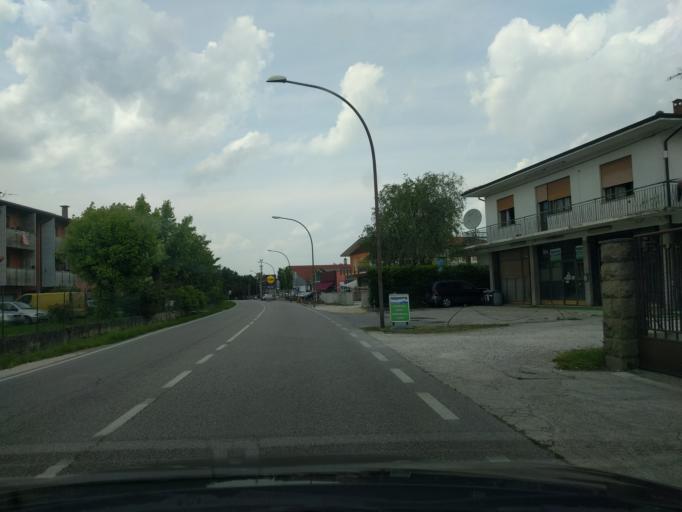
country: IT
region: Veneto
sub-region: Provincia di Rovigo
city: Lendinara
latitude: 45.0873
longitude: 11.6045
